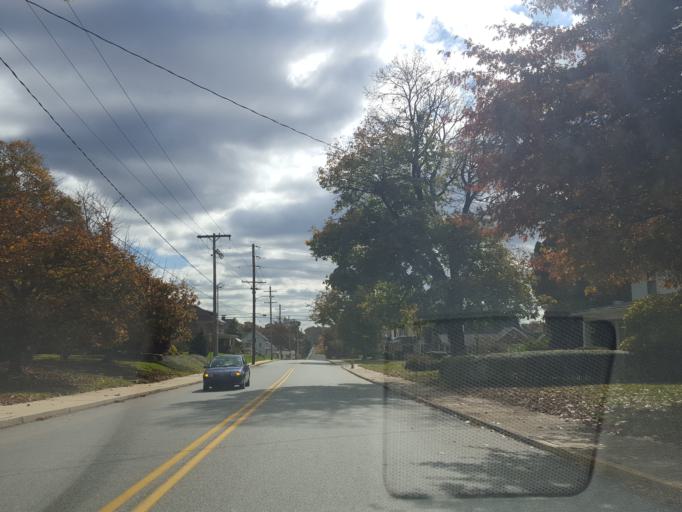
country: US
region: Pennsylvania
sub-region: York County
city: Red Lion
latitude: 39.8947
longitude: -76.5994
